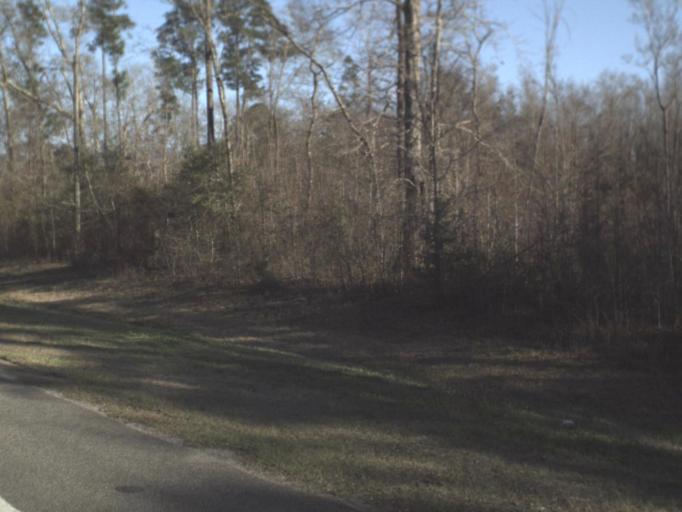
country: US
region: Florida
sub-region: Jackson County
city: Sneads
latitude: 30.7192
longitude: -85.0284
